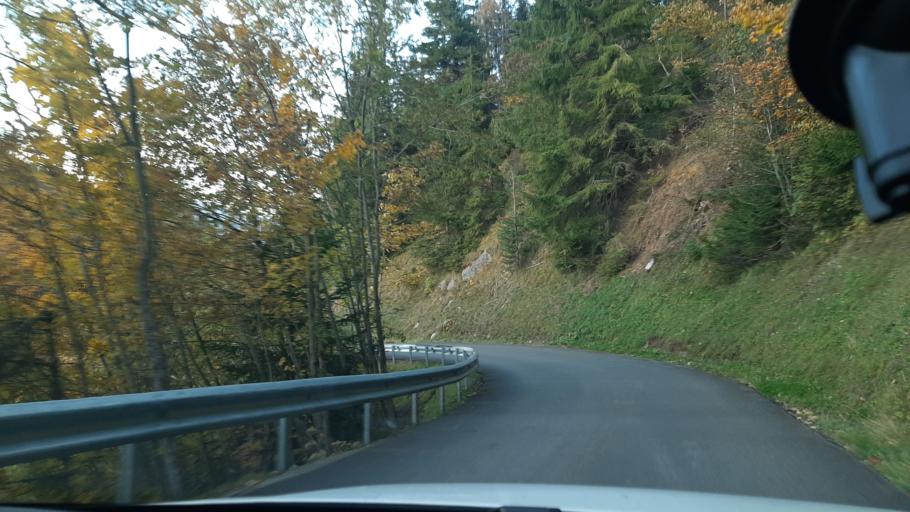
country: FR
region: Rhone-Alpes
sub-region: Departement de la Savoie
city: Saint-Jean-de-Maurienne
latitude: 45.1984
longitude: 6.3102
